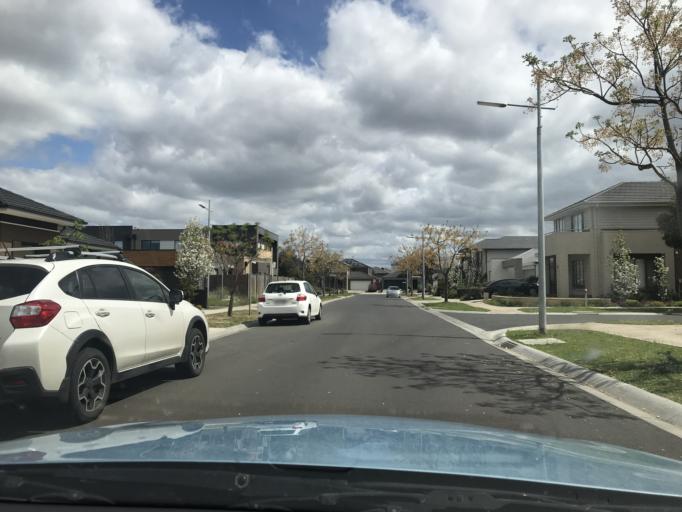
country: AU
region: Victoria
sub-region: Wyndham
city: Williams Landing
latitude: -37.8562
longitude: 144.7520
